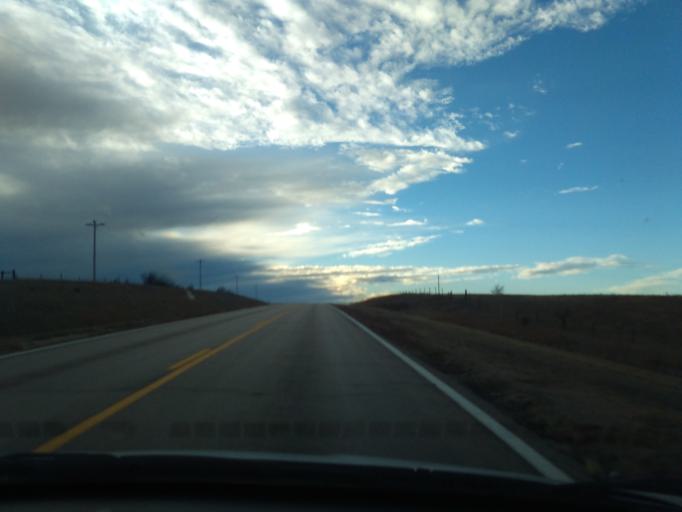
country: US
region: Nebraska
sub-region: Phelps County
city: Holdrege
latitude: 40.3073
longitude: -99.3506
